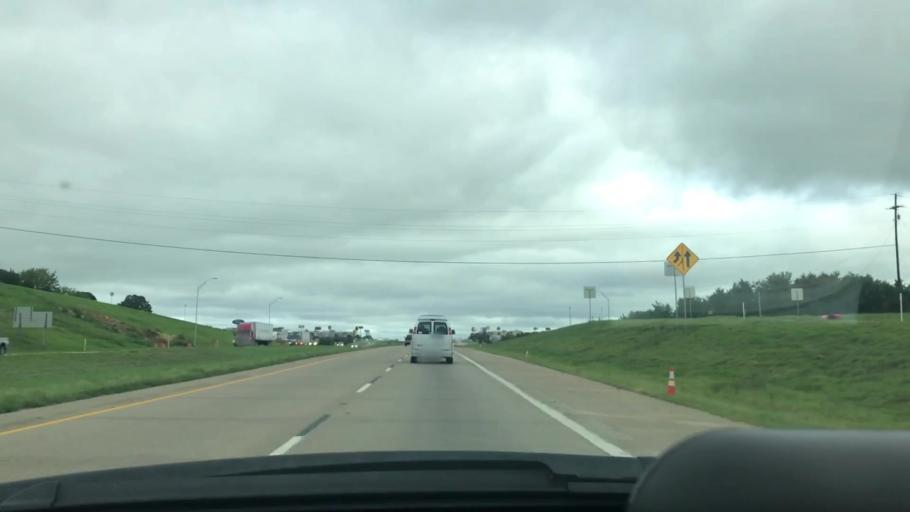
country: US
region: Texas
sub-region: Grayson County
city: Denison
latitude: 33.7514
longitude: -96.5852
